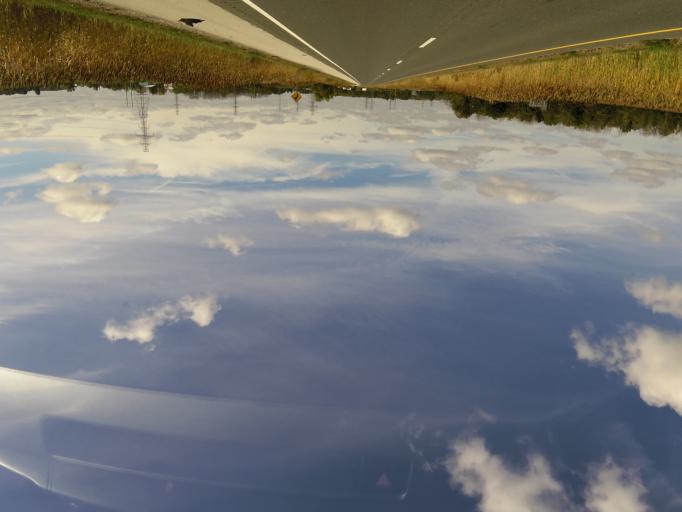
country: CA
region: Ontario
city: London
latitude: 42.9043
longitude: -81.2555
